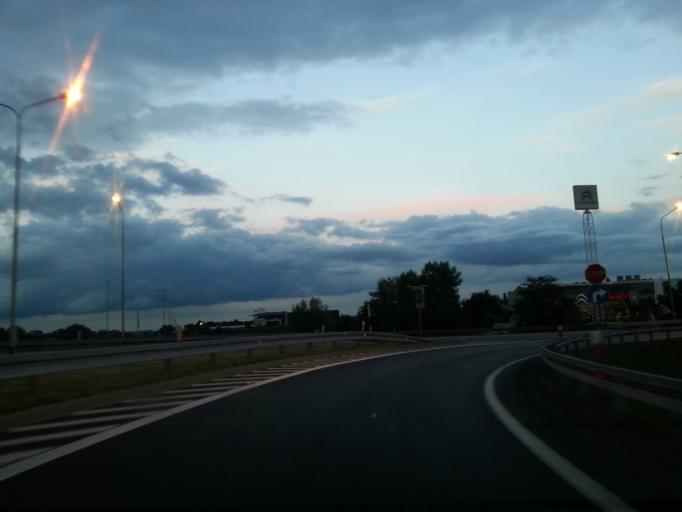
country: PL
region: Lower Silesian Voivodeship
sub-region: Powiat wroclawski
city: Bielany Wroclawskie
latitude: 51.0486
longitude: 16.9711
